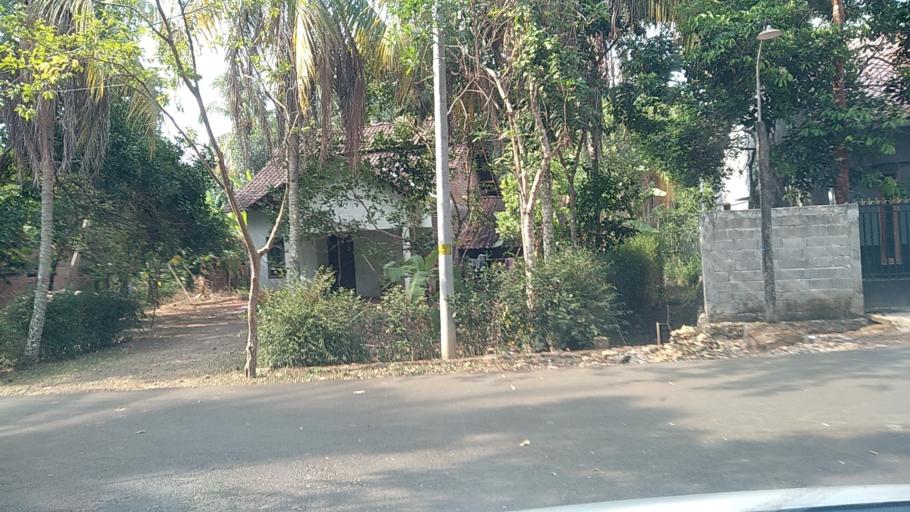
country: ID
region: Central Java
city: Ungaran
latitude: -7.0857
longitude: 110.3967
